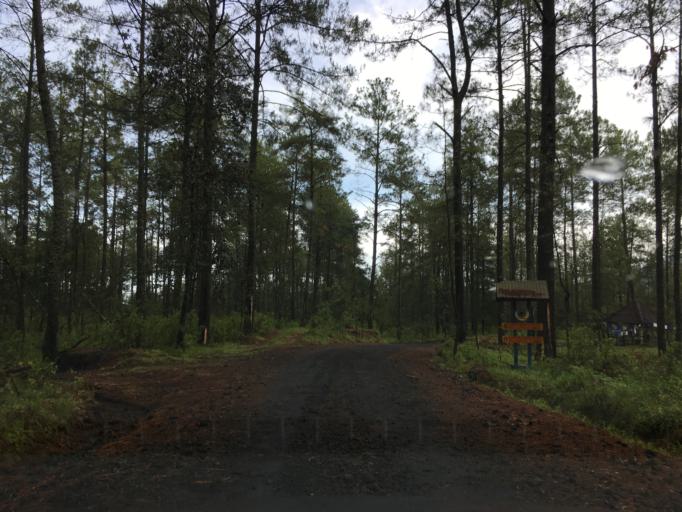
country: MX
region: Michoacan
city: Angahuan
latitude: 19.4923
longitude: -102.2082
